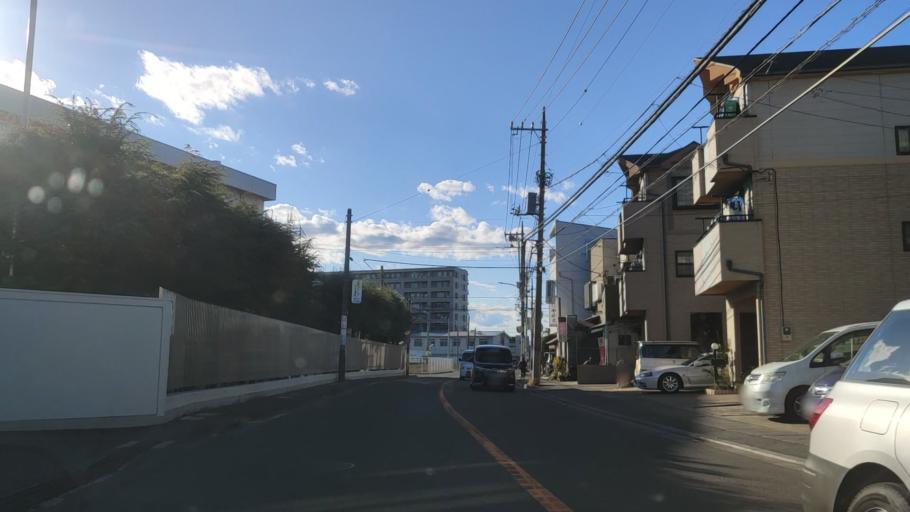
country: JP
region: Tokyo
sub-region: Machida-shi
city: Machida
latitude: 35.5184
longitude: 139.5496
